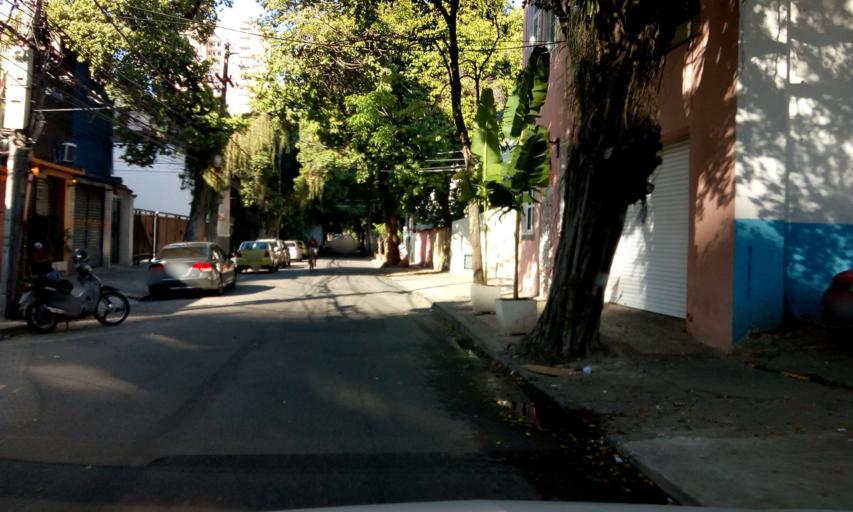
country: BR
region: Rio de Janeiro
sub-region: Rio De Janeiro
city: Rio de Janeiro
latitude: -22.9564
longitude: -43.1815
